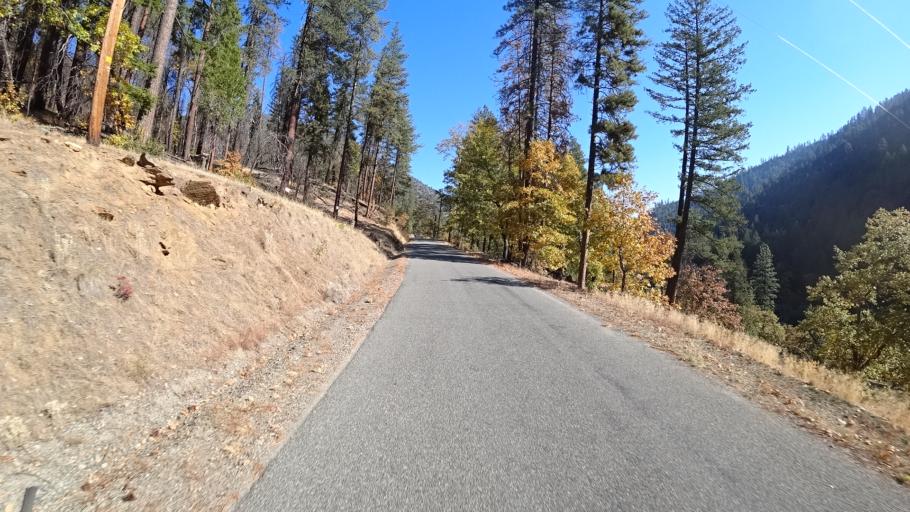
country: US
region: California
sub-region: Siskiyou County
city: Happy Camp
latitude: 41.6893
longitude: -123.0797
